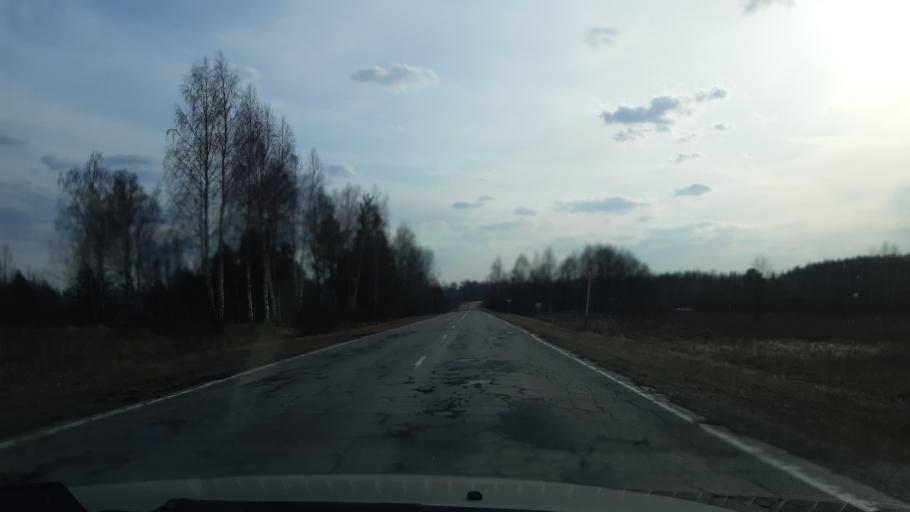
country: RU
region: Vladimir
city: Luknovo
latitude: 56.1815
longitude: 42.0123
